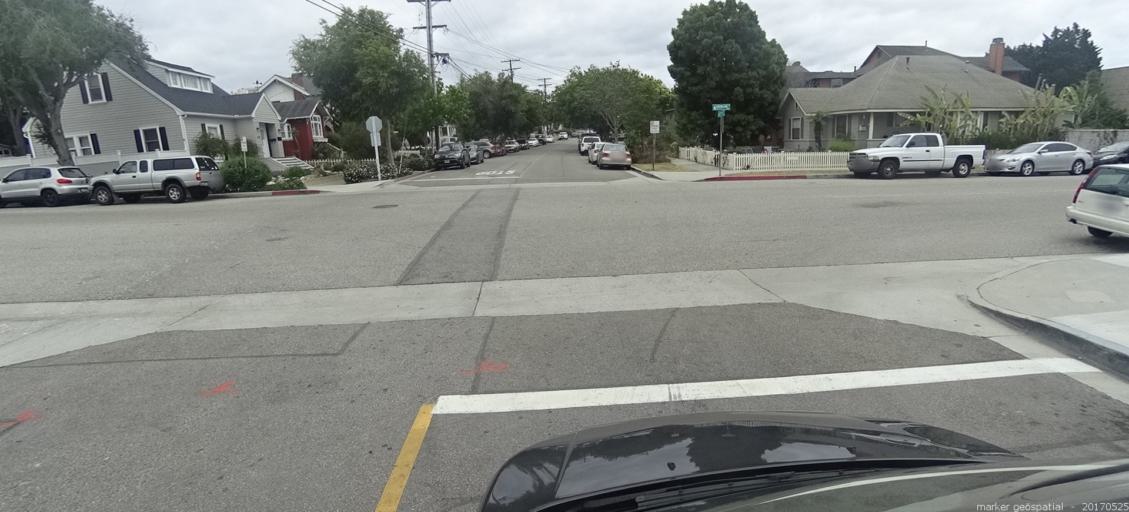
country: US
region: California
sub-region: Los Angeles County
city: Redondo Beach
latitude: 33.8479
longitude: -118.3872
